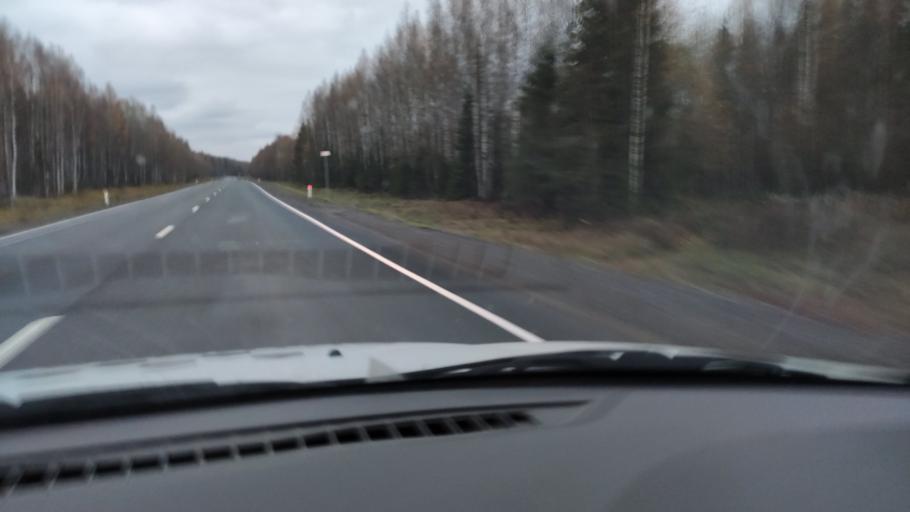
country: RU
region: Kirov
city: Kostino
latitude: 58.8174
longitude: 52.9556
